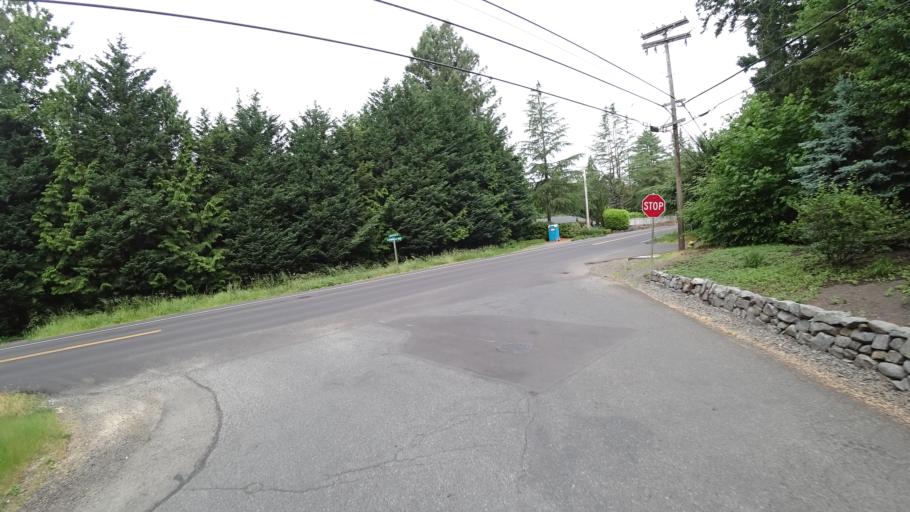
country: US
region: Oregon
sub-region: Clackamas County
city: Lake Oswego
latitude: 45.4343
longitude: -122.6668
